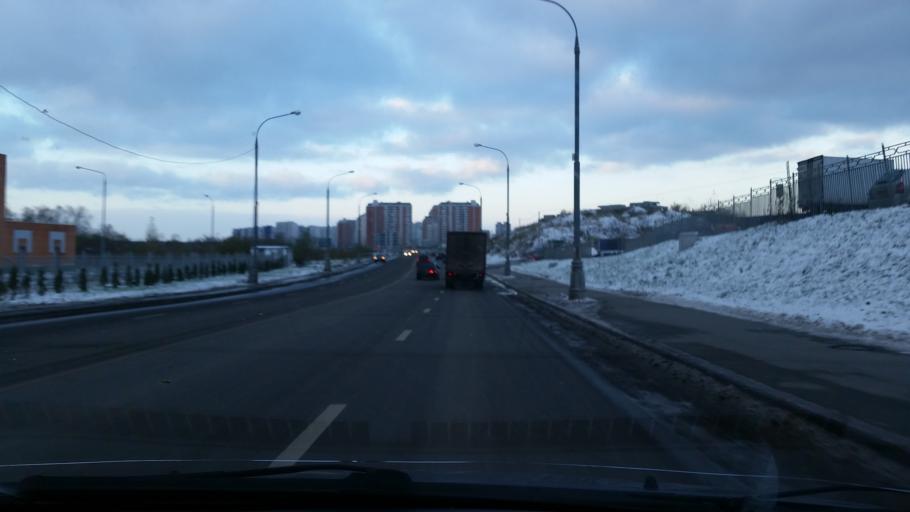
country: RU
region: Moscow
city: Vagonoremont
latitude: 55.9144
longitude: 37.5369
